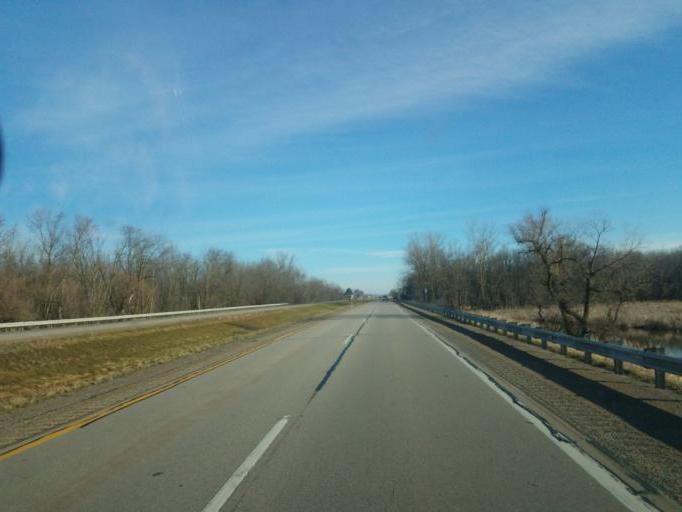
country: US
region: Michigan
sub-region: Clinton County
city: Saint Johns
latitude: 43.1450
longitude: -84.5633
